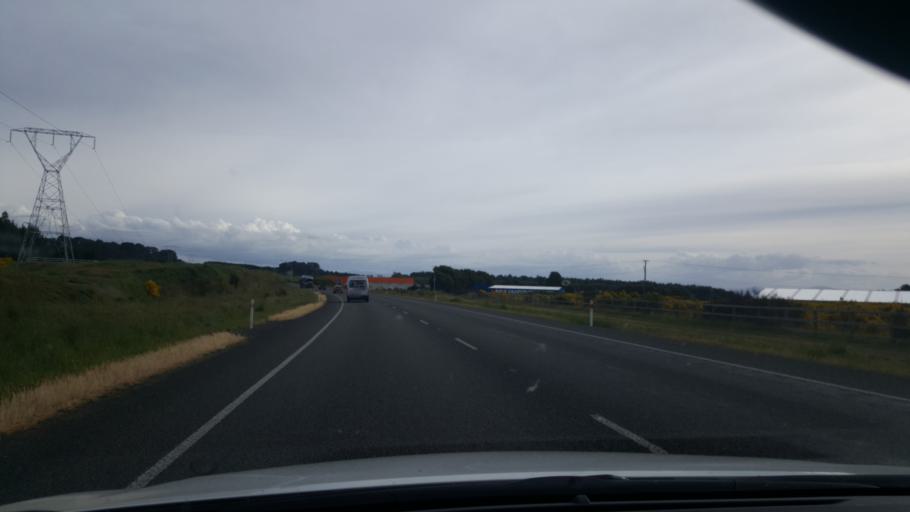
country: NZ
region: Waikato
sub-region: Taupo District
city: Taupo
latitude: -38.6984
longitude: 176.1124
